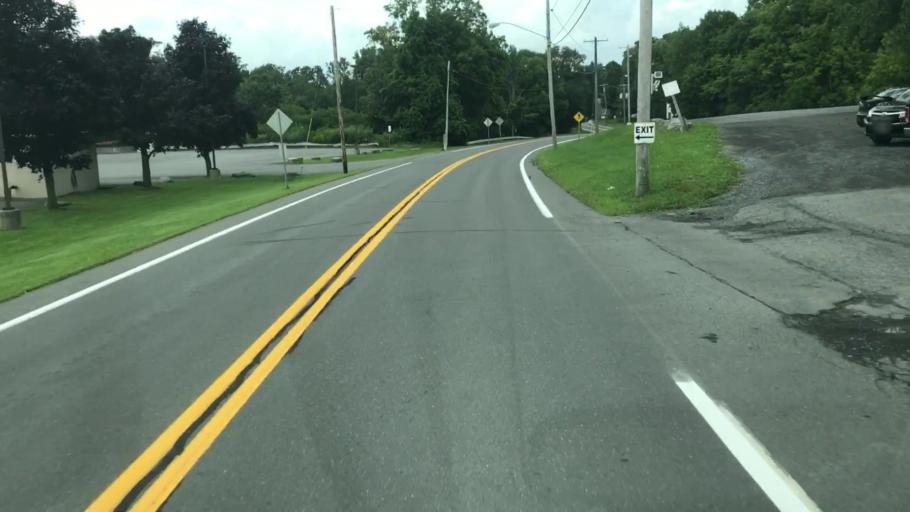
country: US
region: New York
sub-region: Onondaga County
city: Elbridge
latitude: 42.9950
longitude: -76.4576
